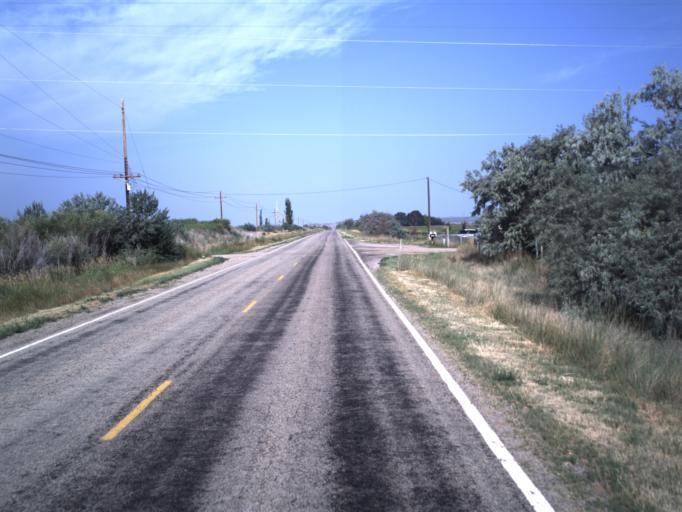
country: US
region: Utah
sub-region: Duchesne County
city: Roosevelt
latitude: 40.2580
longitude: -110.1610
